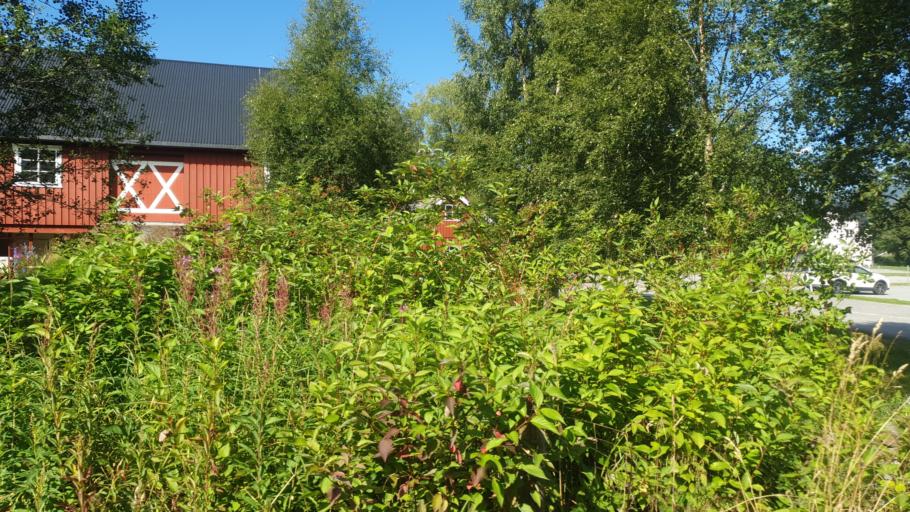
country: NO
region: Sor-Trondelag
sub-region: Orkdal
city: Orkanger
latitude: 63.2855
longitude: 9.8407
